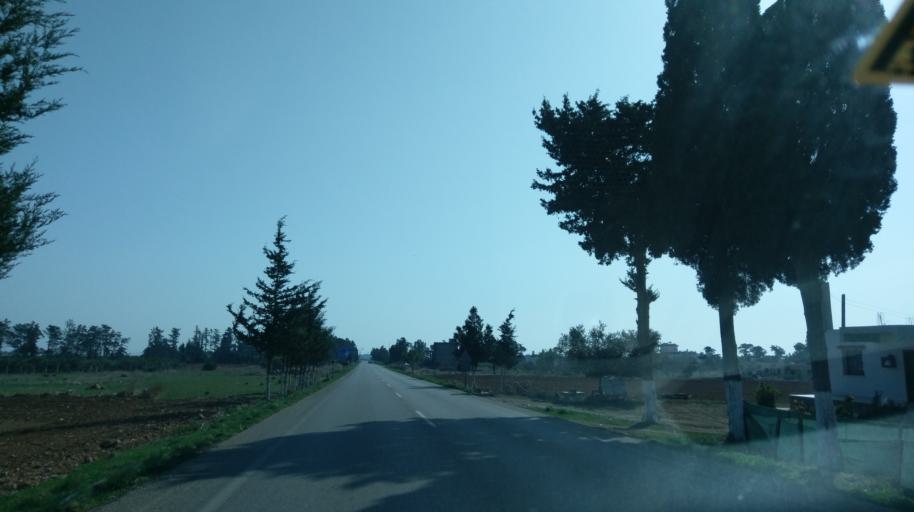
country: CY
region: Ammochostos
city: Leonarisso
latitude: 35.4759
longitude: 34.1433
